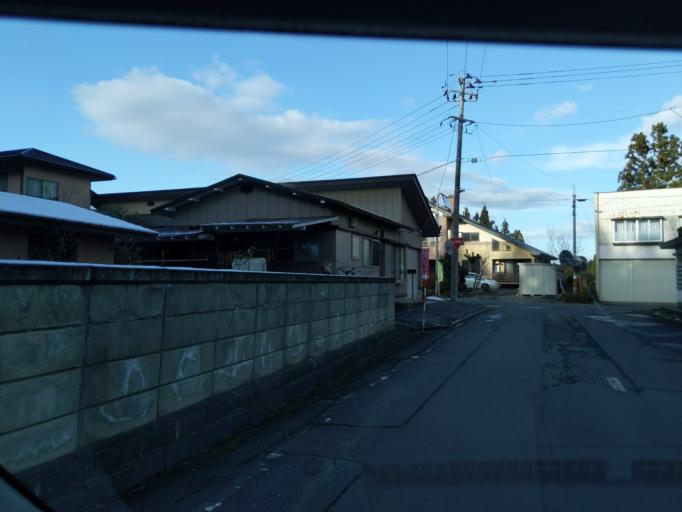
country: JP
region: Iwate
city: Kitakami
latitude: 39.2349
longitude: 141.0509
